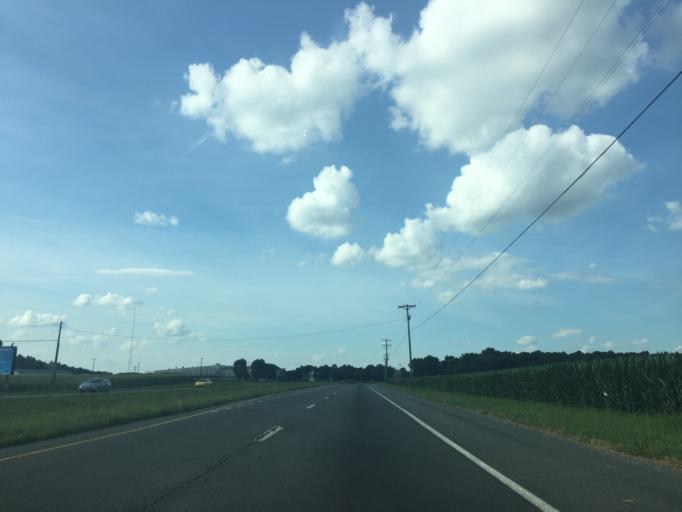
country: US
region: Delaware
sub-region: Sussex County
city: Bridgeville
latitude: 38.7874
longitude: -75.5909
